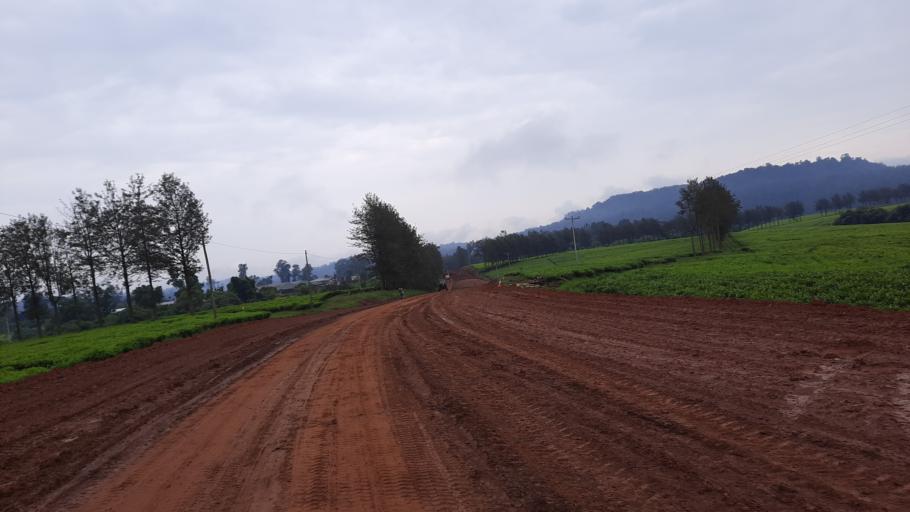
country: ET
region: Oromiya
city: Gore
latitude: 7.8566
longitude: 35.4755
